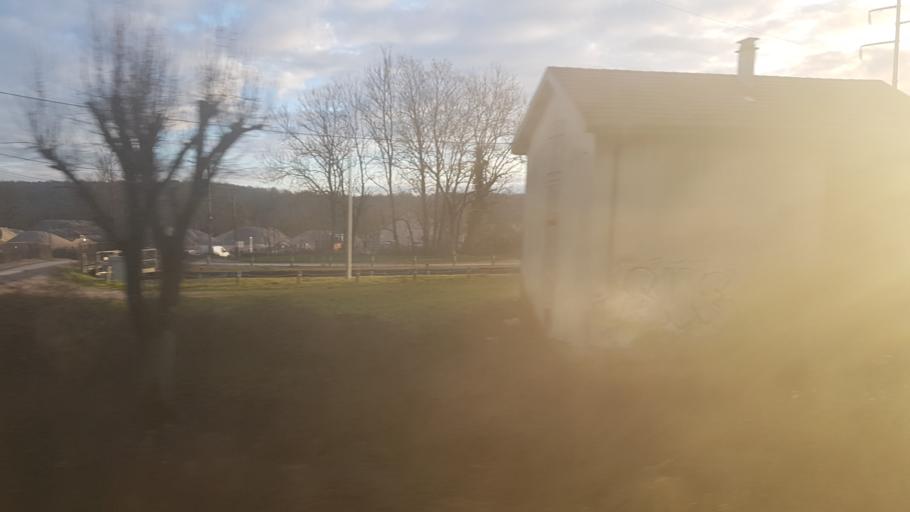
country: FR
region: Lorraine
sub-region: Departement des Vosges
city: Nomexy
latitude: 48.2992
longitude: 6.3945
